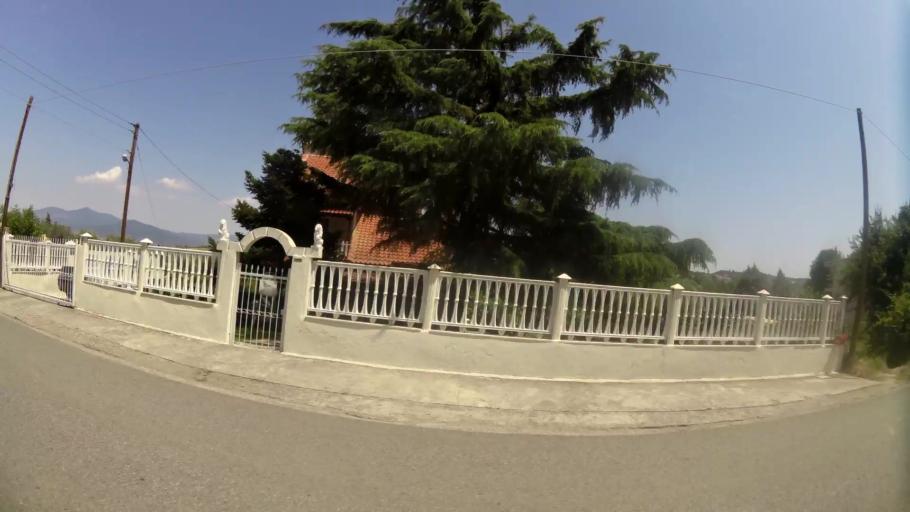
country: GR
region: Central Macedonia
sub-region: Nomos Thessalonikis
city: Trilofos
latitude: 40.4745
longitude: 22.9728
